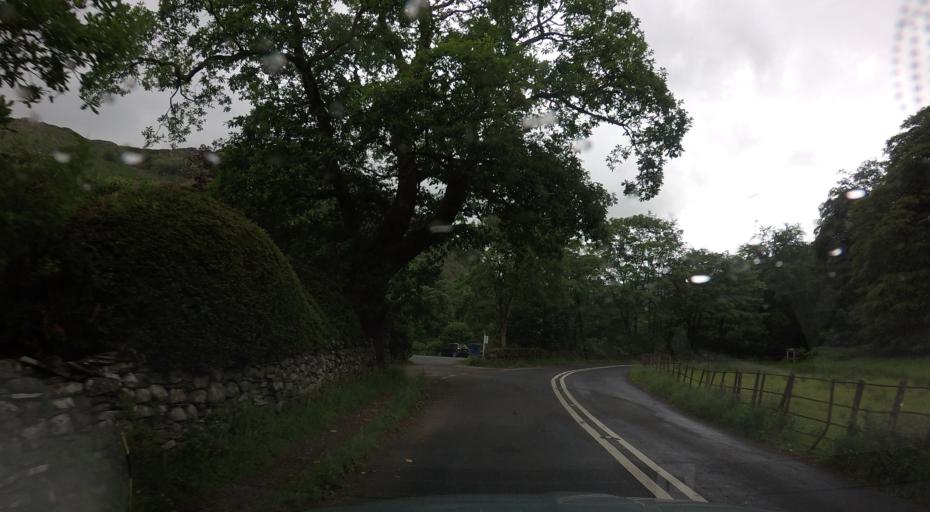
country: GB
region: England
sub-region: Cumbria
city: Keswick
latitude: 54.5230
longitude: -3.1467
